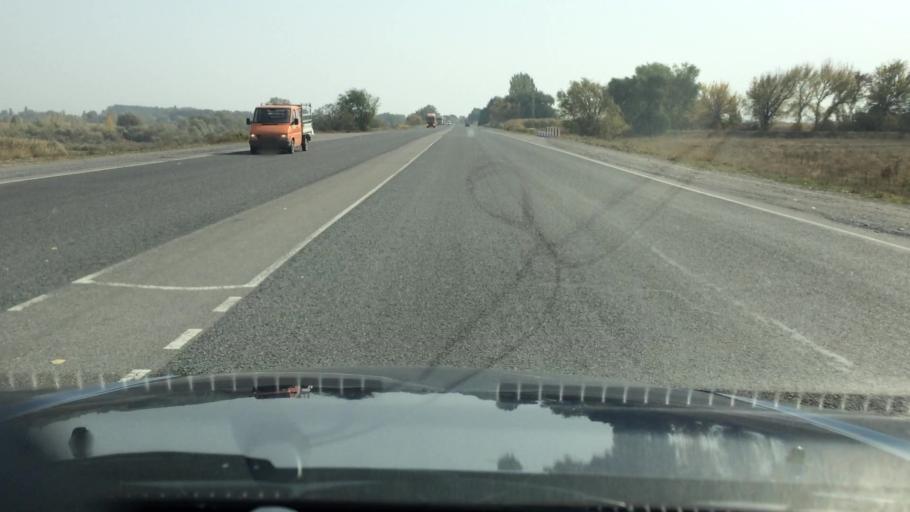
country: KG
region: Chuy
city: Kant
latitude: 42.9449
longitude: 74.9613
